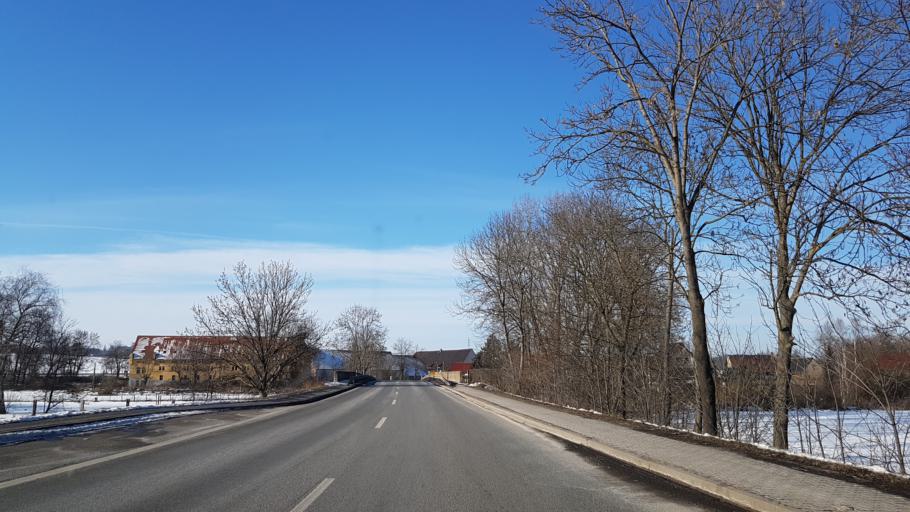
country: DE
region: Thuringia
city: Nobitz
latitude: 50.9825
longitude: 12.4785
